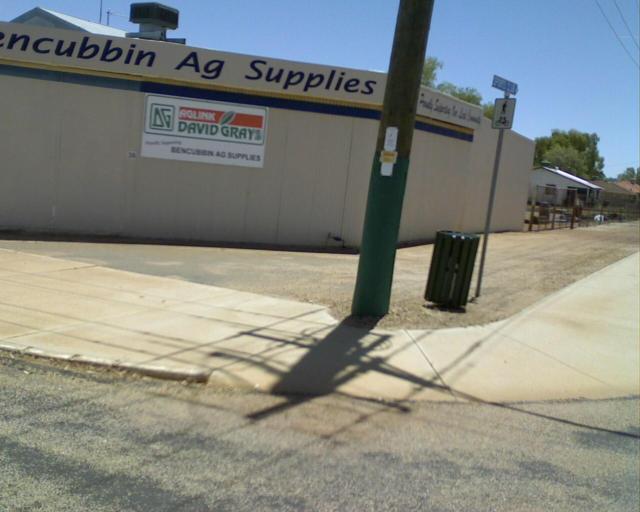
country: AU
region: Western Australia
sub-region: Merredin
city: Merredin
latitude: -30.8097
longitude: 117.8613
